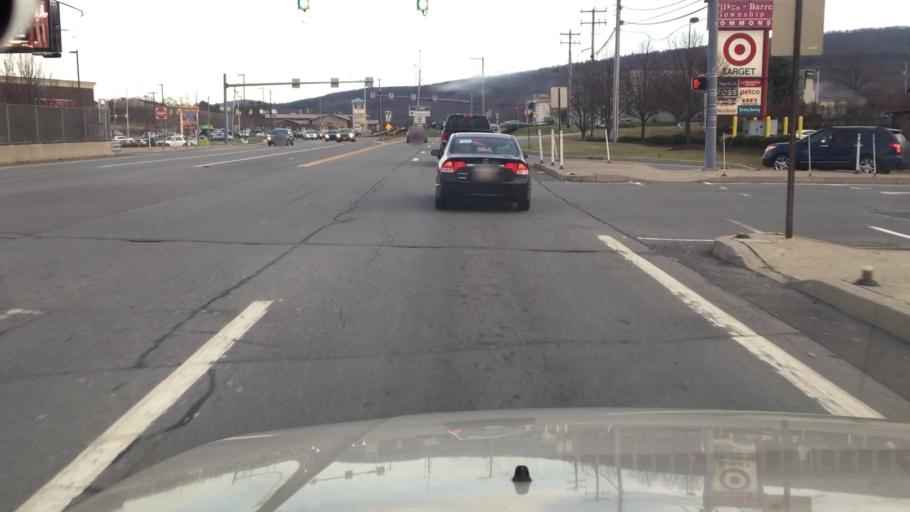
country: US
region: Pennsylvania
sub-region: Luzerne County
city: Georgetown
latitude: 41.2432
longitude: -75.8442
